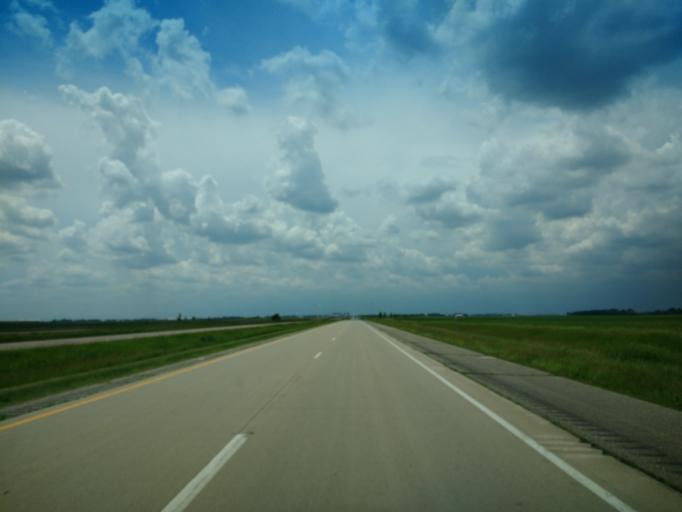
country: US
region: Minnesota
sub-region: Nobles County
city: Worthington
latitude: 43.7383
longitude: -95.4108
